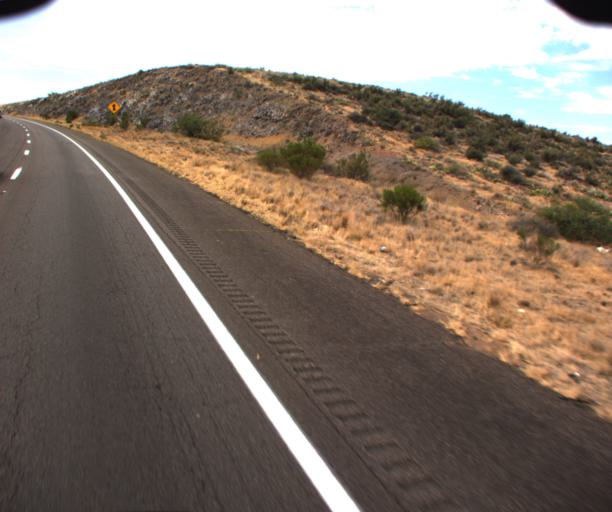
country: US
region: Arizona
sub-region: Yavapai County
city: Cordes Lakes
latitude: 34.2341
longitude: -112.1172
